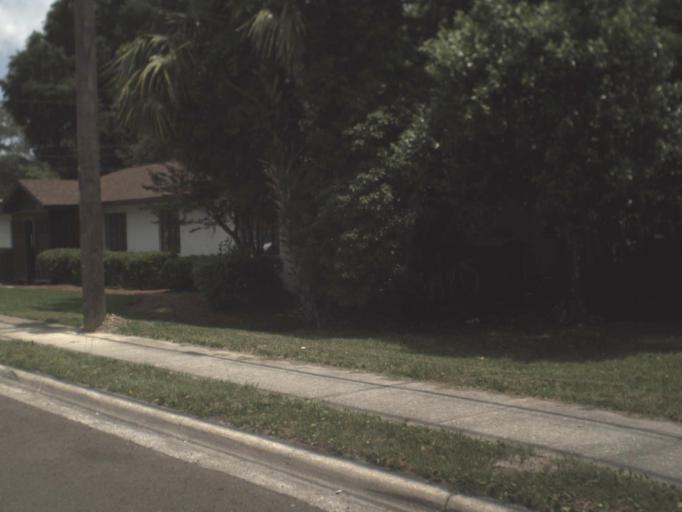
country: US
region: Florida
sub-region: Duval County
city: Jacksonville
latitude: 30.3045
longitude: -81.7305
